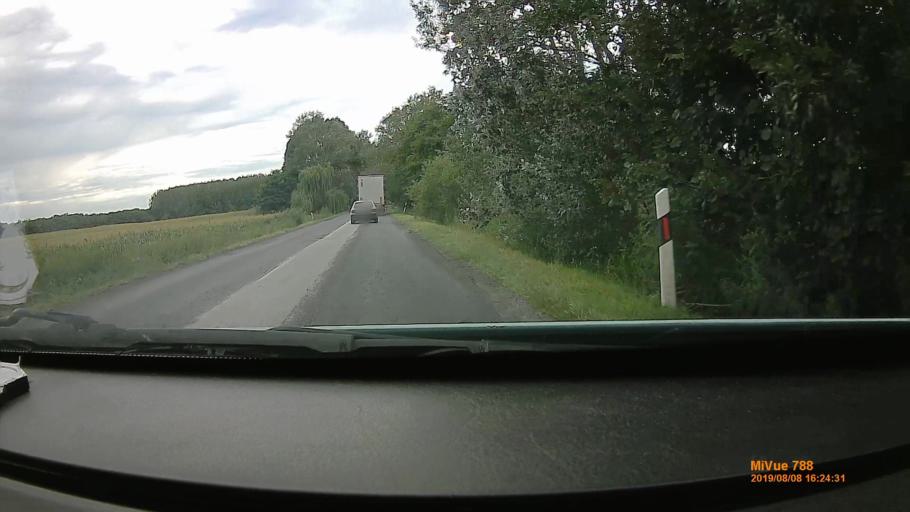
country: HU
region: Szabolcs-Szatmar-Bereg
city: Hodasz
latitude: 47.9686
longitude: 22.2258
